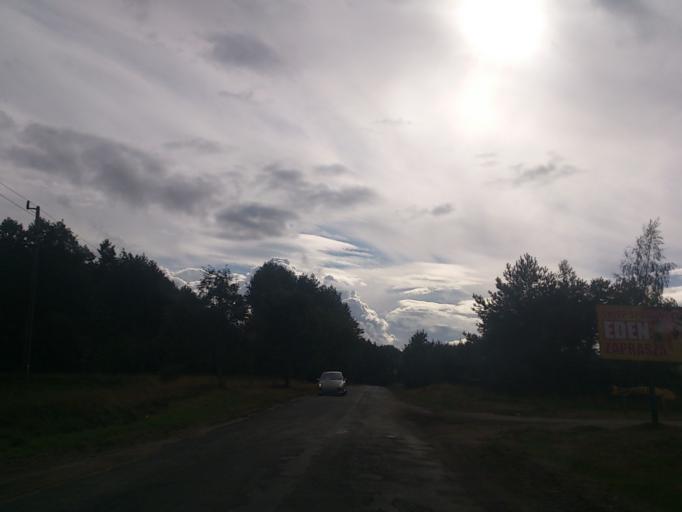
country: PL
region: Greater Poland Voivodeship
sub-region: Powiat poznanski
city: Kobylnica
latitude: 52.5175
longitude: 17.1393
